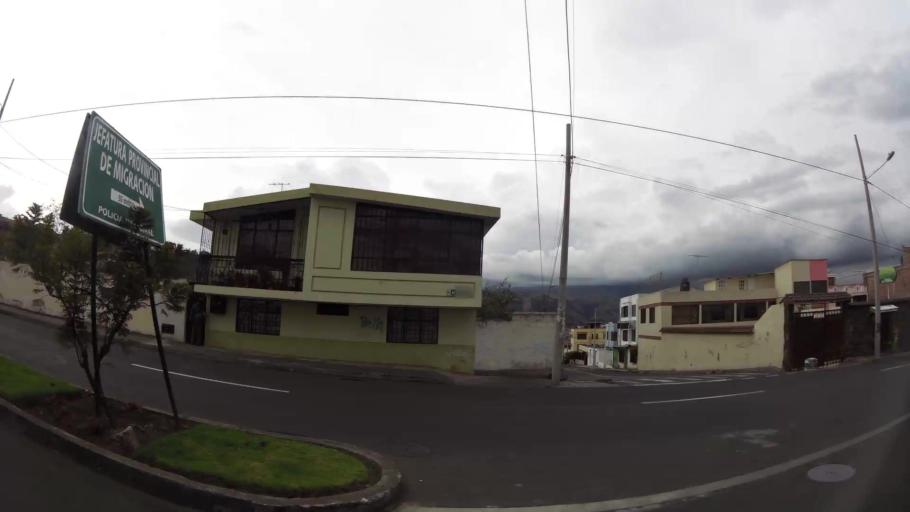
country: EC
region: Tungurahua
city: Ambato
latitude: -1.2731
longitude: -78.6345
